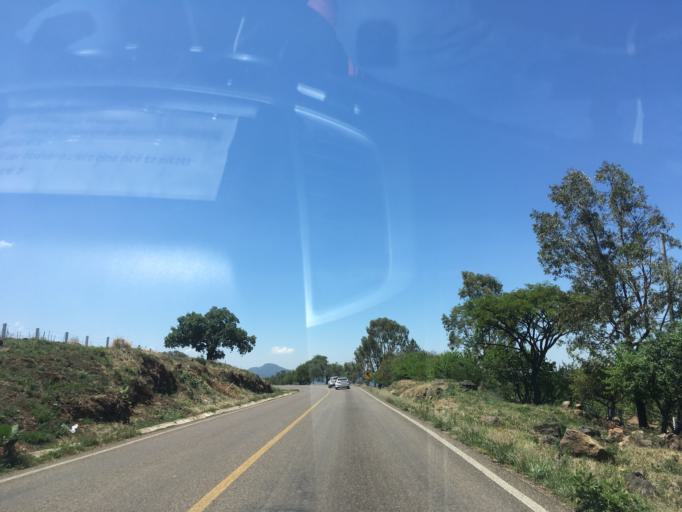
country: MX
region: Michoacan
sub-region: Tuxpan
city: La Soledad
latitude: 19.5040
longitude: -100.4652
